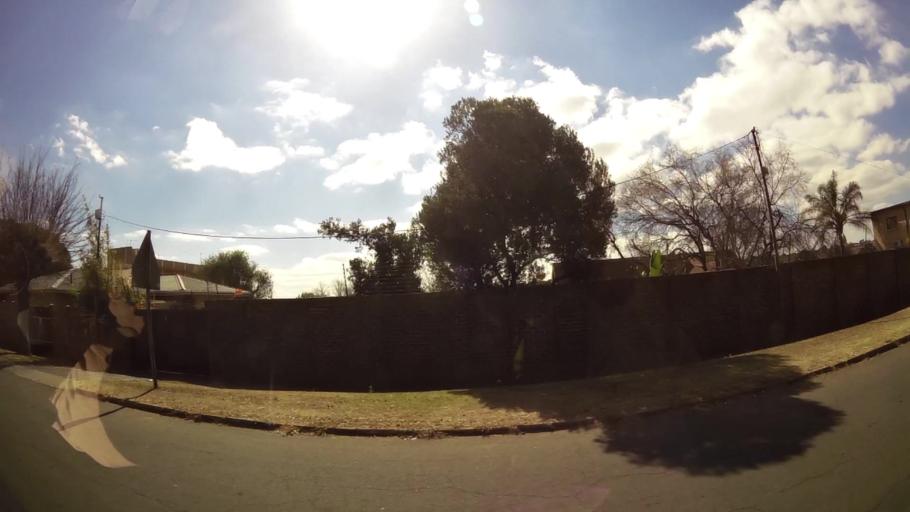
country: ZA
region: Gauteng
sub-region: West Rand District Municipality
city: Krugersdorp
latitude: -26.1089
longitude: 27.7843
